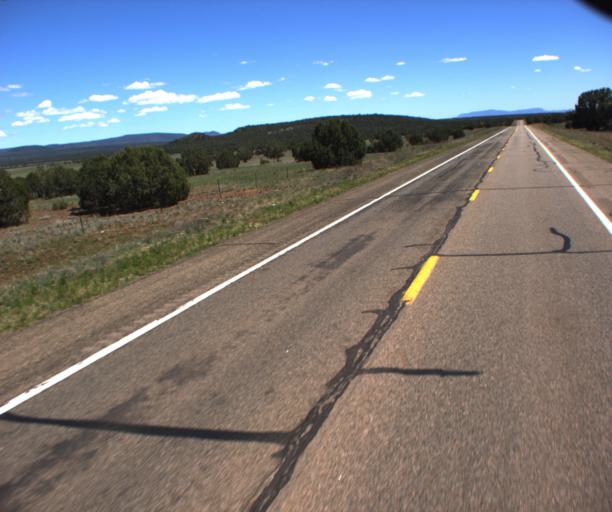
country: US
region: Arizona
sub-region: Yavapai County
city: Paulden
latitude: 35.1487
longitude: -112.4487
